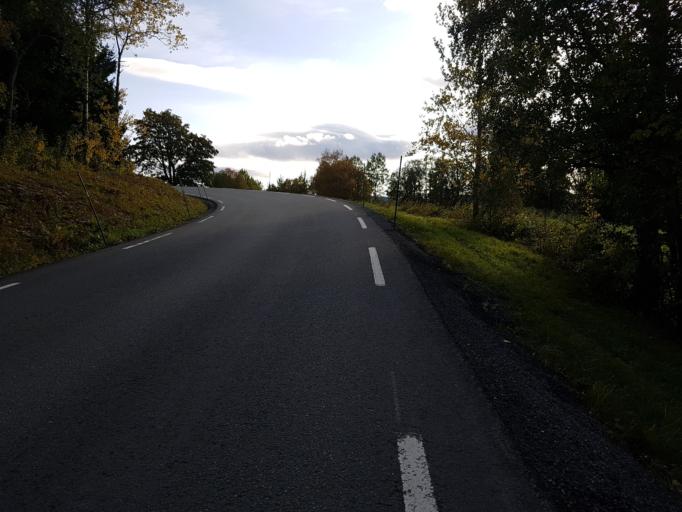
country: NO
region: Sor-Trondelag
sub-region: Malvik
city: Malvik
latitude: 63.3644
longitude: 10.6234
